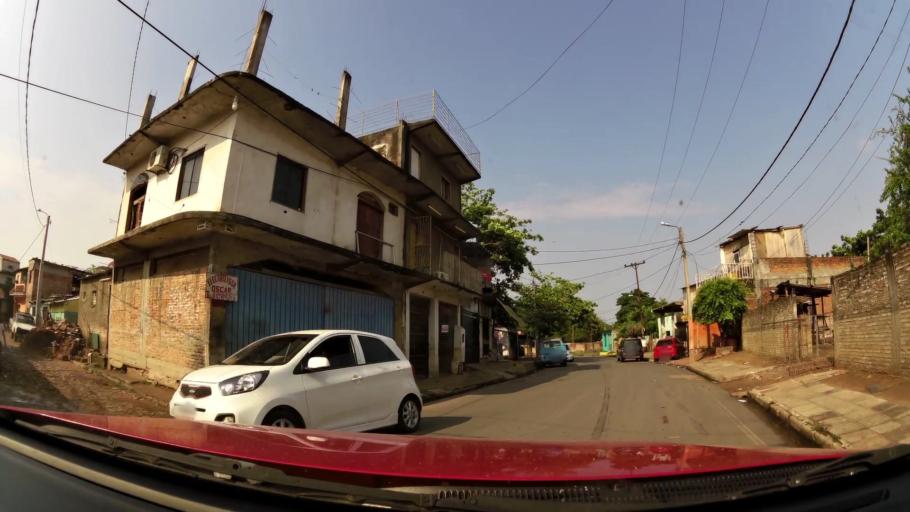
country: PY
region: Asuncion
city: Asuncion
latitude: -25.3015
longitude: -57.6648
